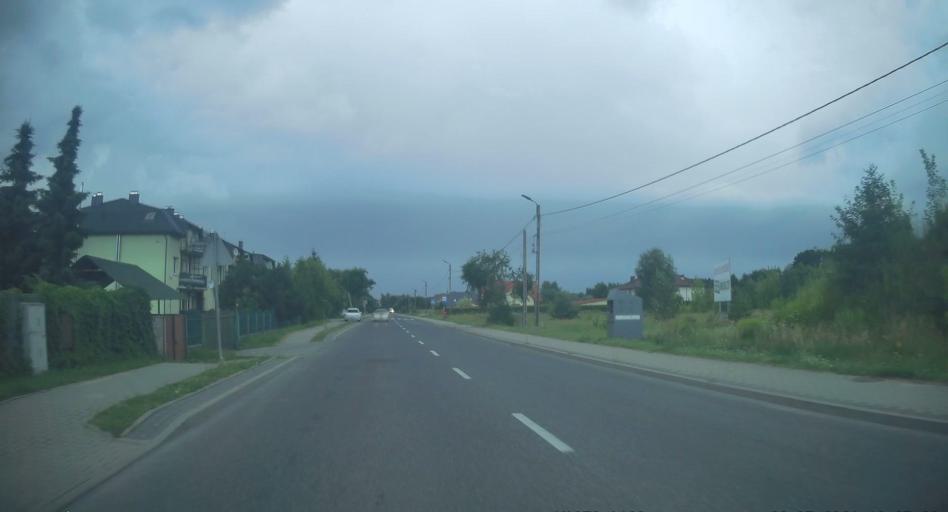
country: PL
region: Lodz Voivodeship
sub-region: Powiat rawski
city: Rawa Mazowiecka
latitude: 51.7518
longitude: 20.2240
